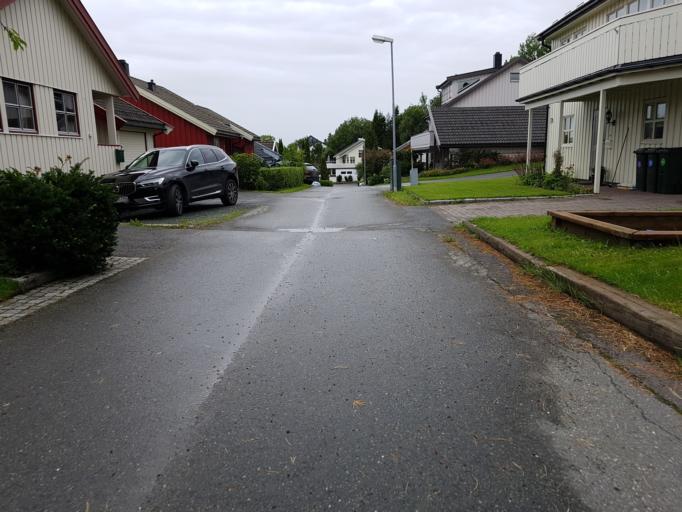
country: NO
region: Sor-Trondelag
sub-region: Trondheim
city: Trondheim
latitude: 63.4053
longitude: 10.4812
